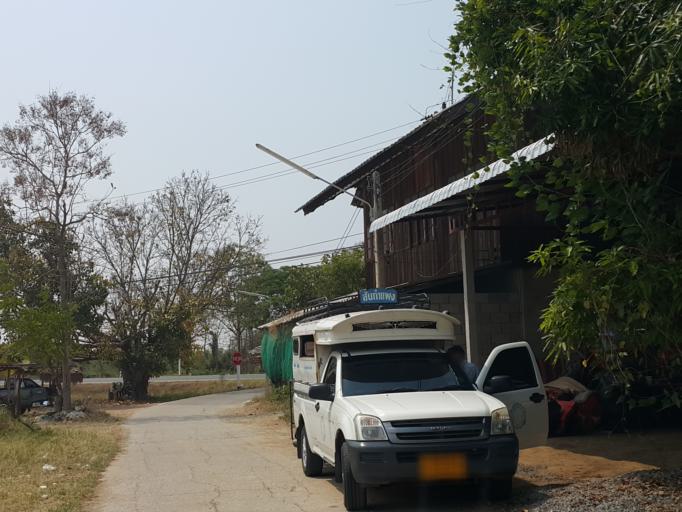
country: TH
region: Chiang Mai
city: San Kamphaeng
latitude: 18.7174
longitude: 99.1172
